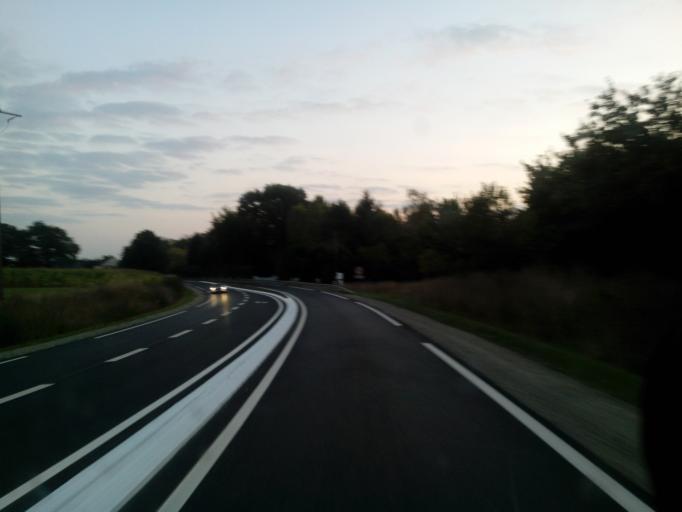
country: FR
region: Brittany
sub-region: Departement d'Ille-et-Vilaine
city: Bedee
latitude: 48.1724
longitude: -1.9439
